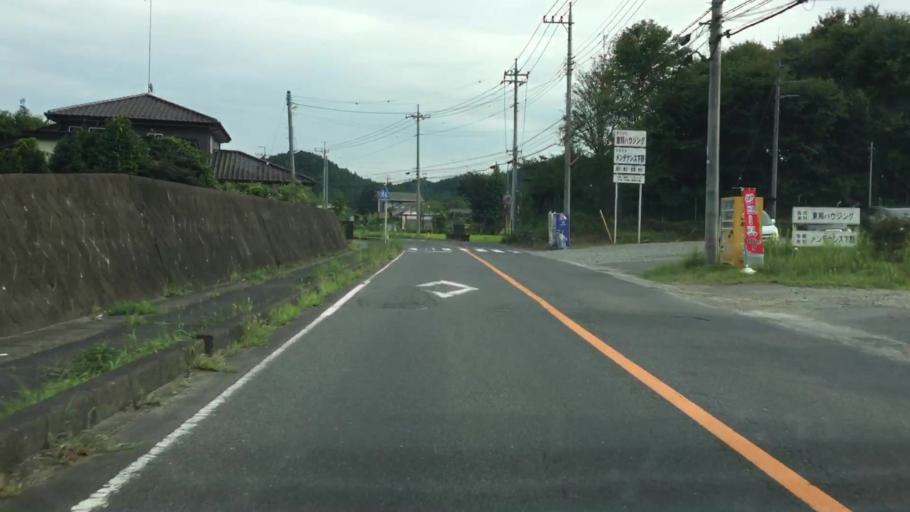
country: JP
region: Tochigi
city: Imaichi
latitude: 36.7469
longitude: 139.7371
